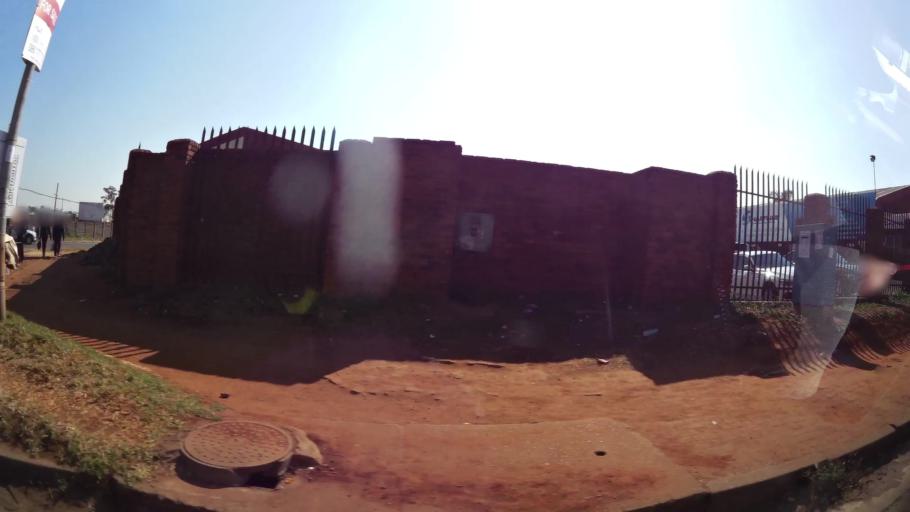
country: ZA
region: Gauteng
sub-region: Ekurhuleni Metropolitan Municipality
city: Boksburg
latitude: -26.1745
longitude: 28.2128
